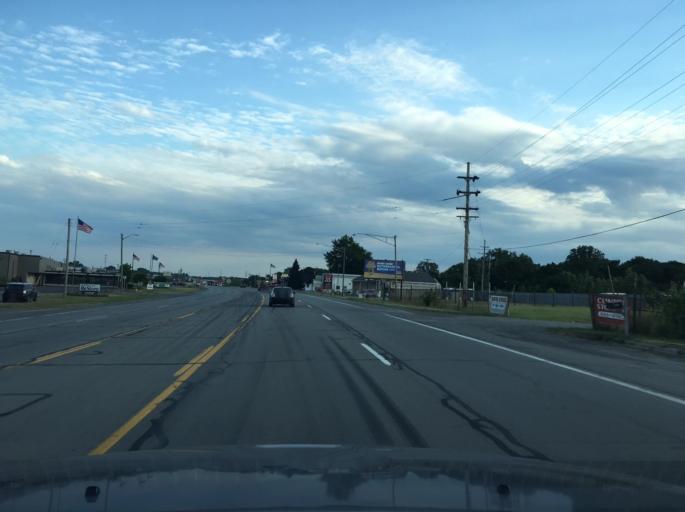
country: US
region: Michigan
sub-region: Macomb County
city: Mount Clemens
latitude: 42.6049
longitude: -82.8985
